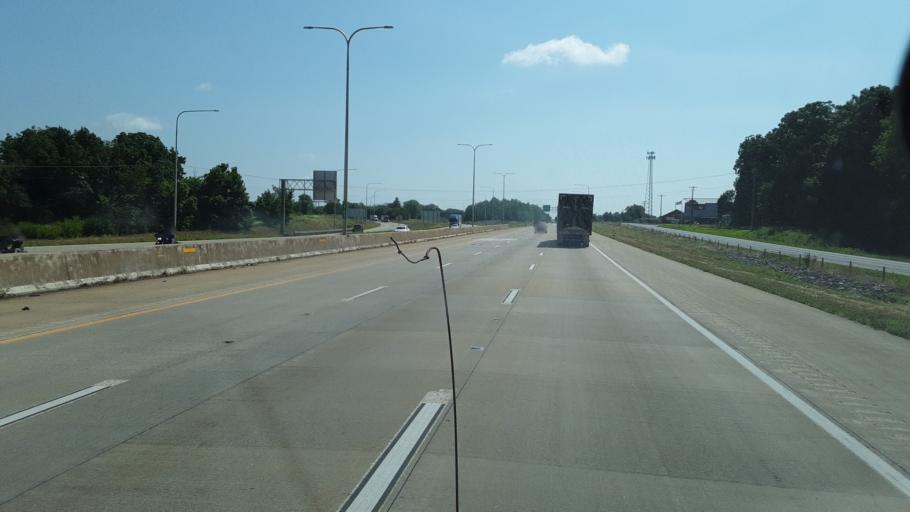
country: US
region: Illinois
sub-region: Effingham County
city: Effingham
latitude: 39.1473
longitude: -88.5185
